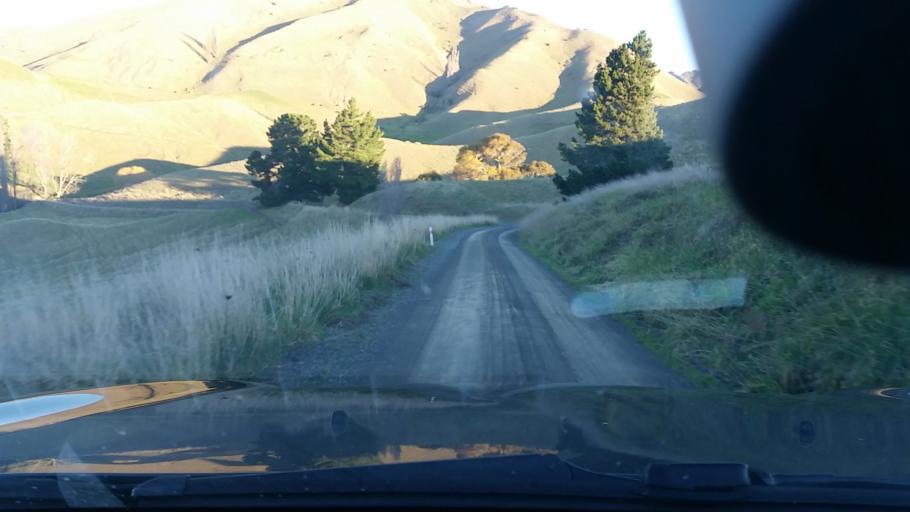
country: NZ
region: Marlborough
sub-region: Marlborough District
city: Blenheim
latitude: -41.7400
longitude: 174.0490
